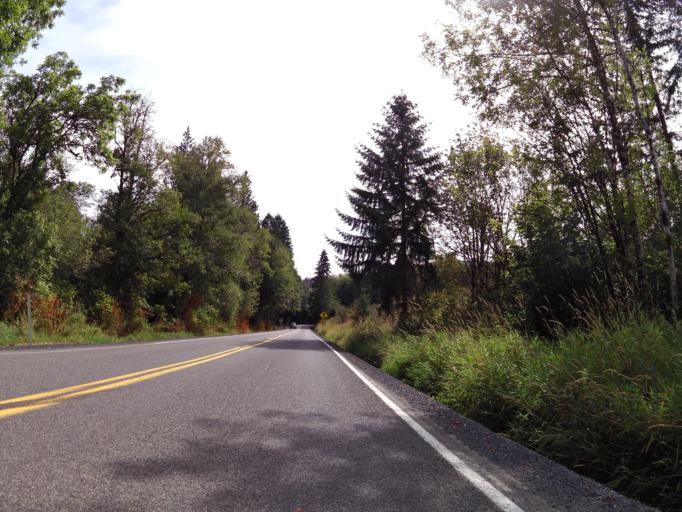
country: US
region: Washington
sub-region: Lewis County
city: Napavine
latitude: 46.5590
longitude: -122.9608
